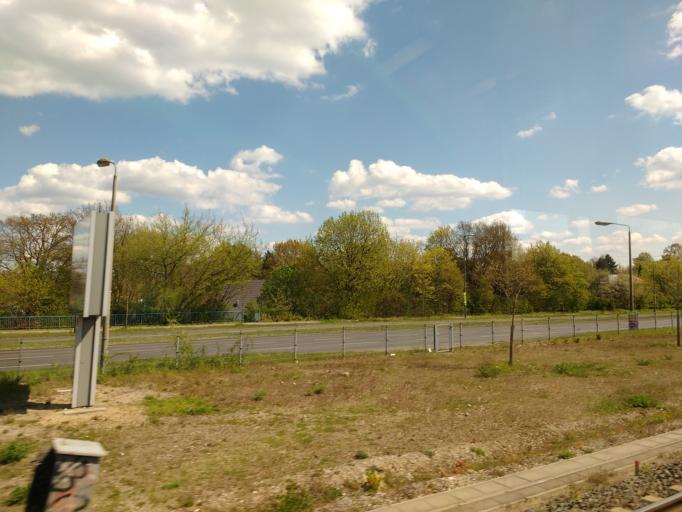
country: DE
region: Berlin
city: Adlershof
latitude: 52.4255
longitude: 13.5553
